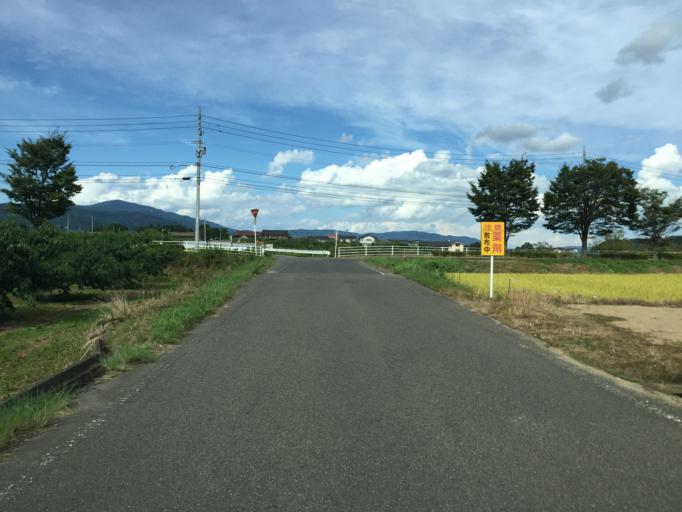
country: JP
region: Fukushima
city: Fukushima-shi
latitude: 37.7968
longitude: 140.4951
